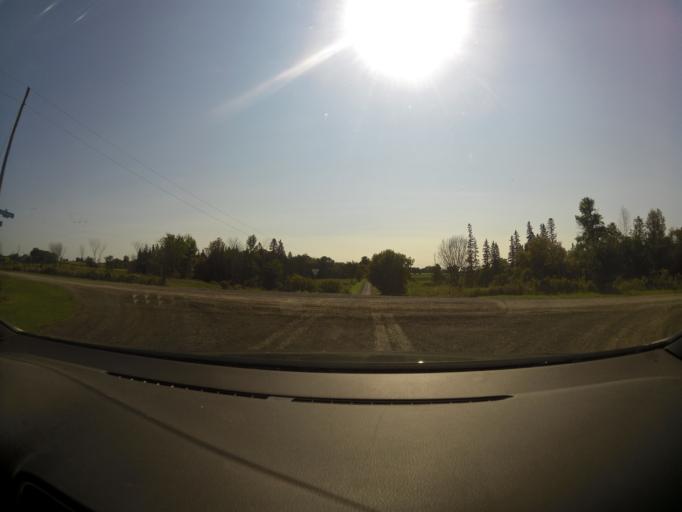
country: CA
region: Ontario
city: Arnprior
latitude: 45.3550
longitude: -76.2605
